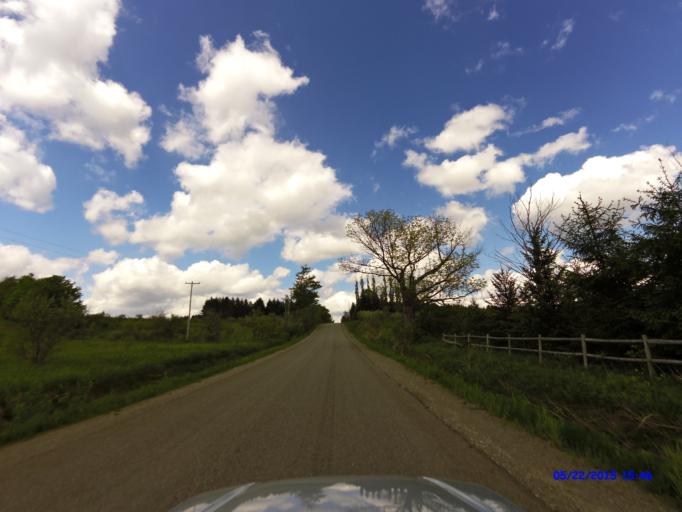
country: US
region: New York
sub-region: Cattaraugus County
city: Franklinville
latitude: 42.3229
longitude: -78.5193
